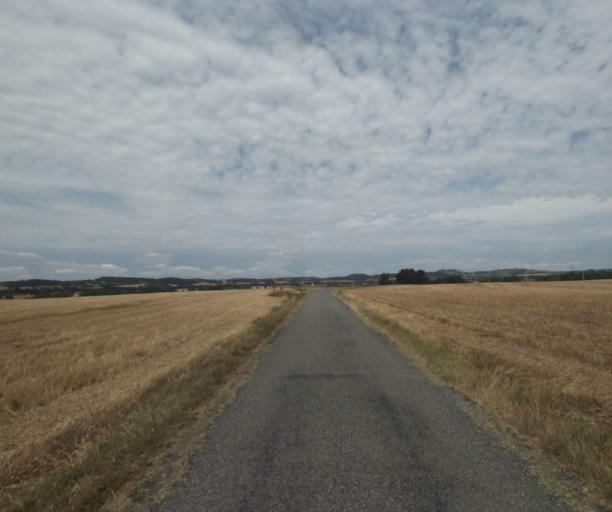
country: FR
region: Midi-Pyrenees
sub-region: Departement de la Haute-Garonne
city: Saint-Felix-Lauragais
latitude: 43.4010
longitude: 1.9077
